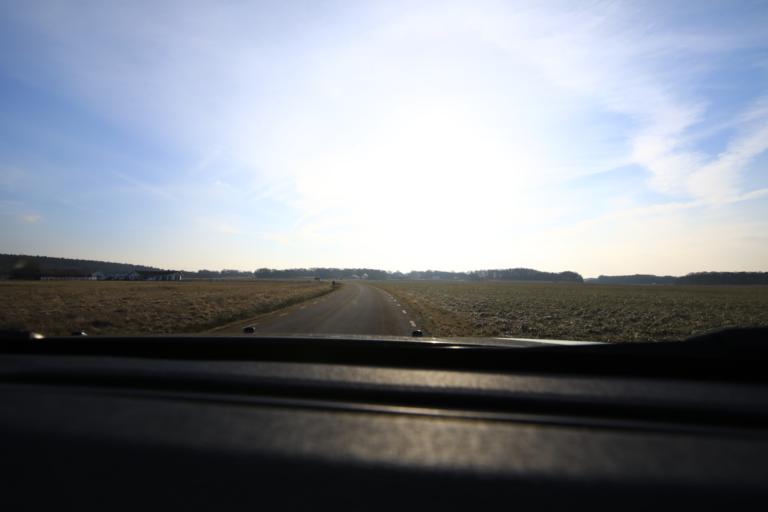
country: SE
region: Halland
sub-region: Varbergs Kommun
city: Varberg
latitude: 57.2006
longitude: 12.2185
